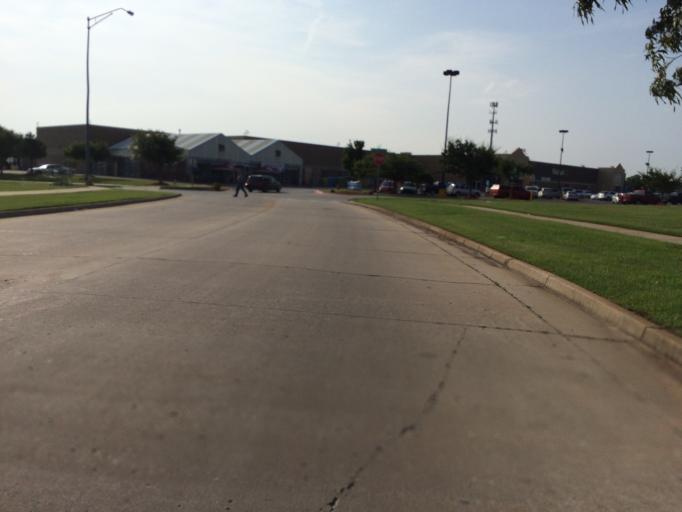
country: US
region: Oklahoma
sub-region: Cleveland County
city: Norman
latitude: 35.2230
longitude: -97.4826
